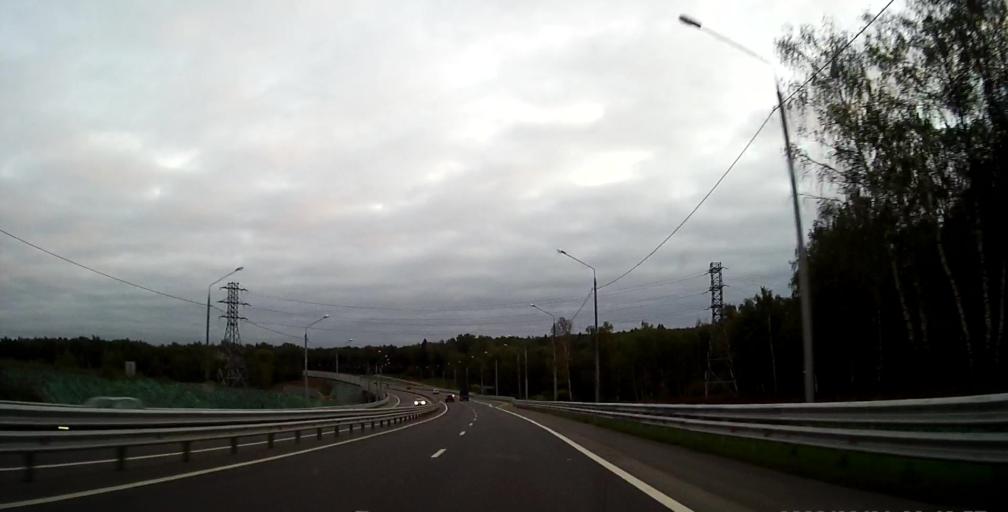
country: RU
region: Moskovskaya
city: Dubrovitsy
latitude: 55.4088
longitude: 37.5017
